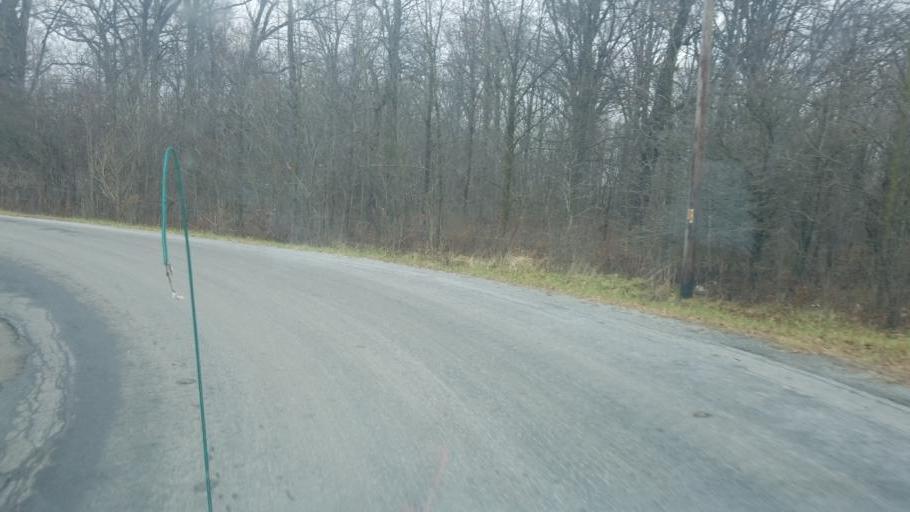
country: US
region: Ohio
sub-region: Hardin County
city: Kenton
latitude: 40.5652
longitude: -83.4676
